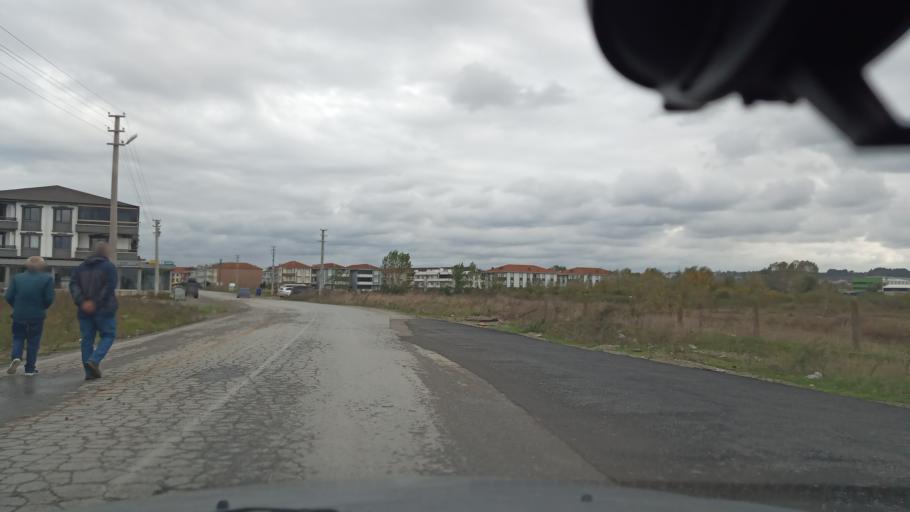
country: TR
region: Sakarya
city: Karasu
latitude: 41.1126
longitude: 30.6763
